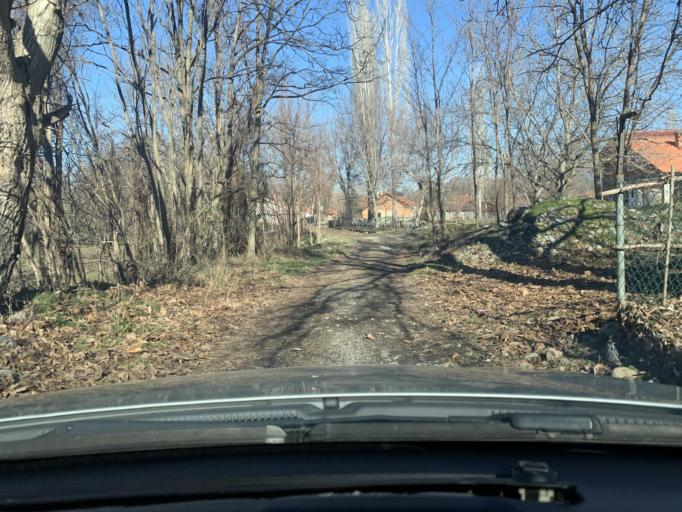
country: MK
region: Demir Kapija
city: Demir Kapija
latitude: 41.3892
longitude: 22.2220
